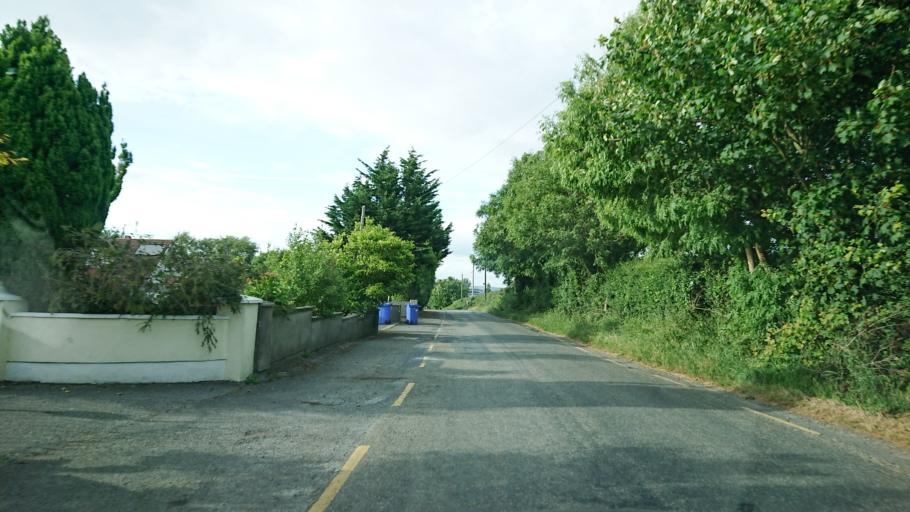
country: IE
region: Munster
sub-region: Waterford
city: Waterford
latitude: 52.2345
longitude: -7.1580
